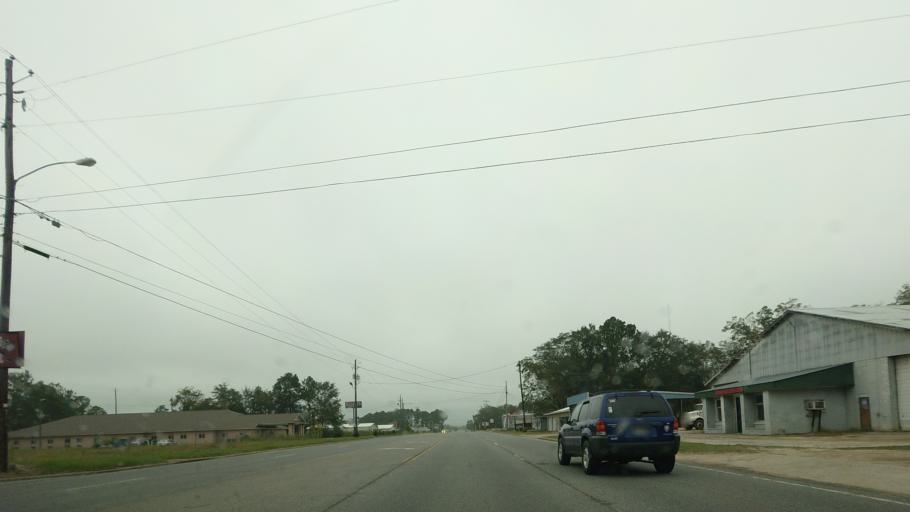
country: US
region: Georgia
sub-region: Irwin County
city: Ocilla
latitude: 31.6180
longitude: -83.2499
